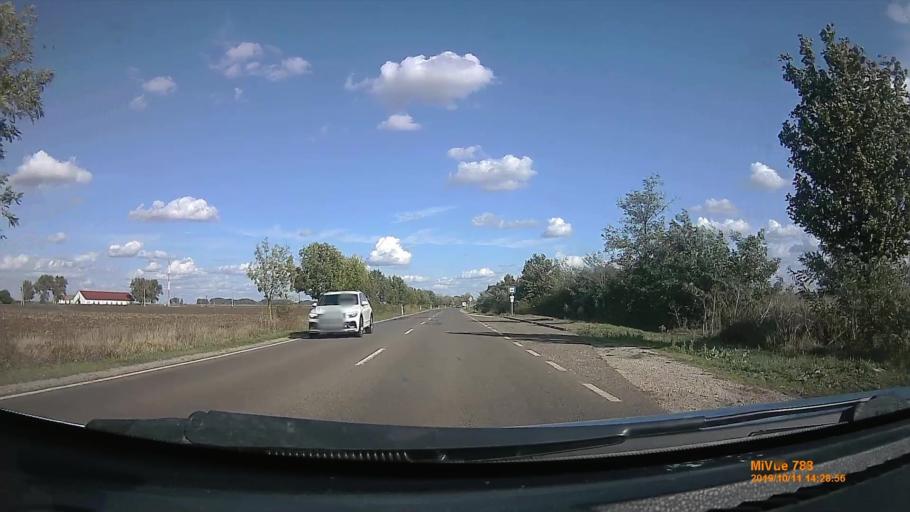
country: HU
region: Hajdu-Bihar
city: Balmazujvaros
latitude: 47.5580
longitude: 21.3753
